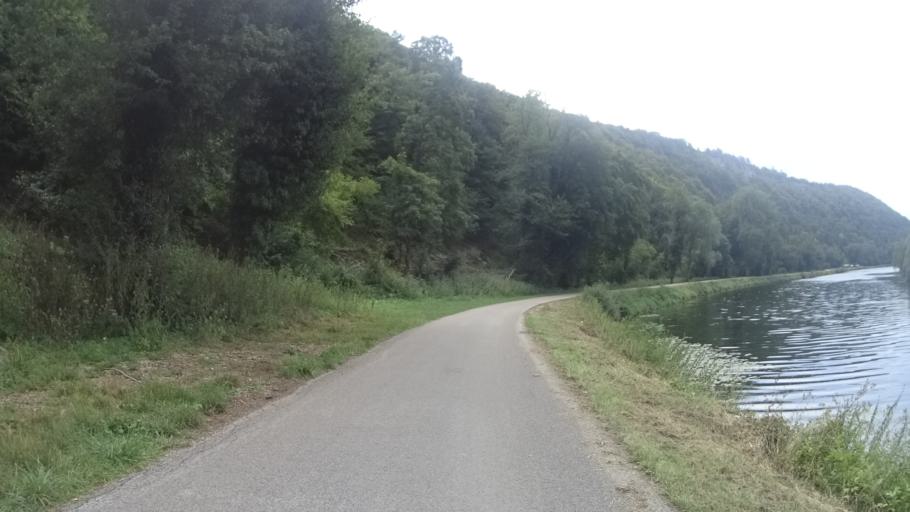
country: FR
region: Franche-Comte
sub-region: Departement du Doubs
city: Baume-les-Dames
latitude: 47.3587
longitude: 6.4190
